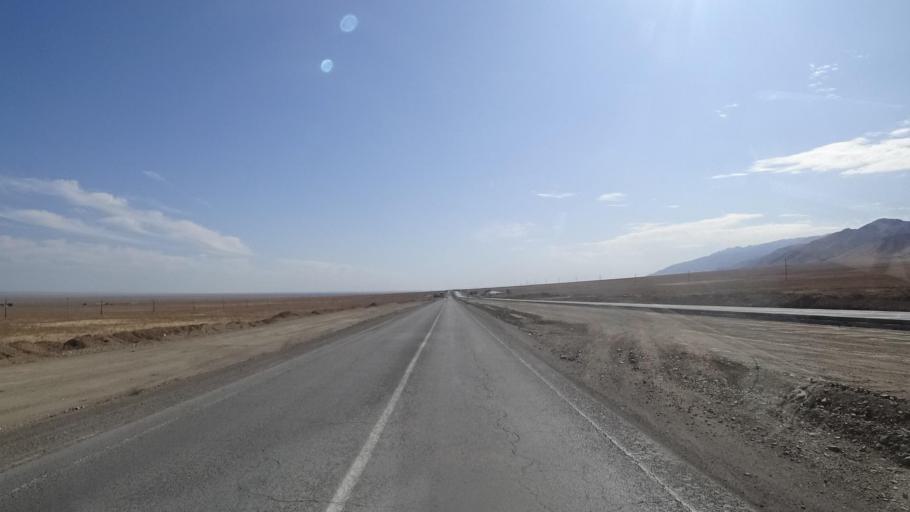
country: KG
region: Chuy
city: Ivanovka
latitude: 43.3860
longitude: 75.1592
